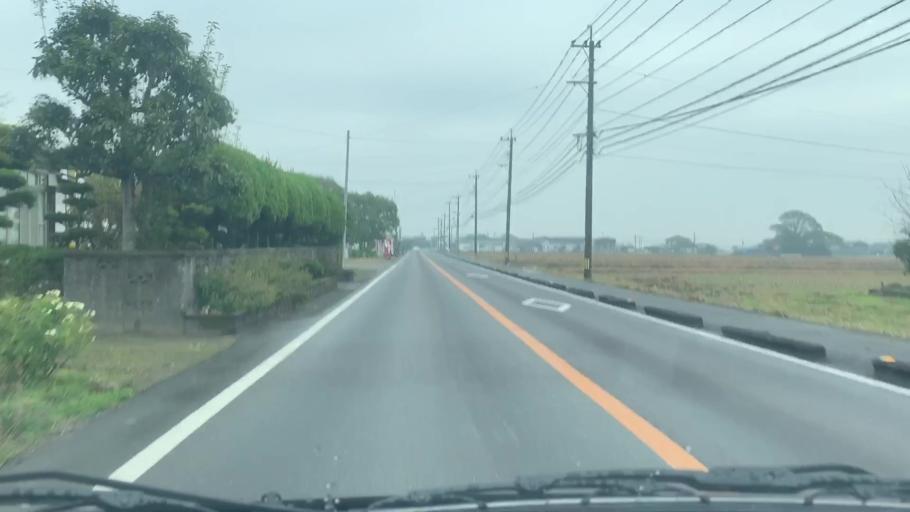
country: JP
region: Saga Prefecture
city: Takeocho-takeo
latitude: 33.1968
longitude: 130.1090
